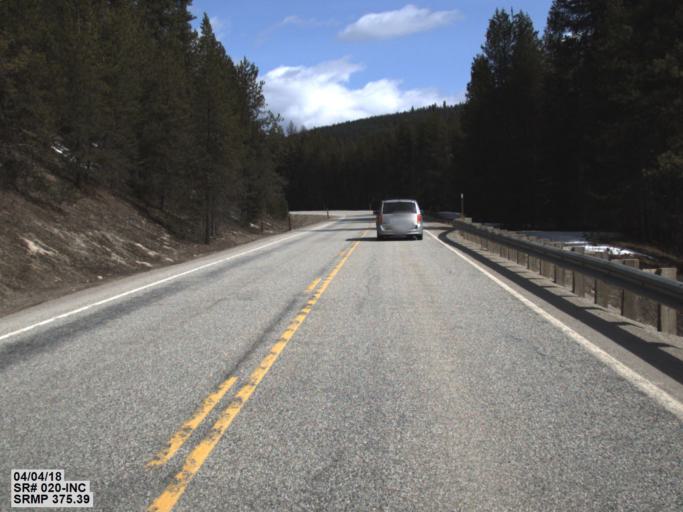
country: US
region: Washington
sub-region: Stevens County
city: Chewelah
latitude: 48.5609
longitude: -117.5562
